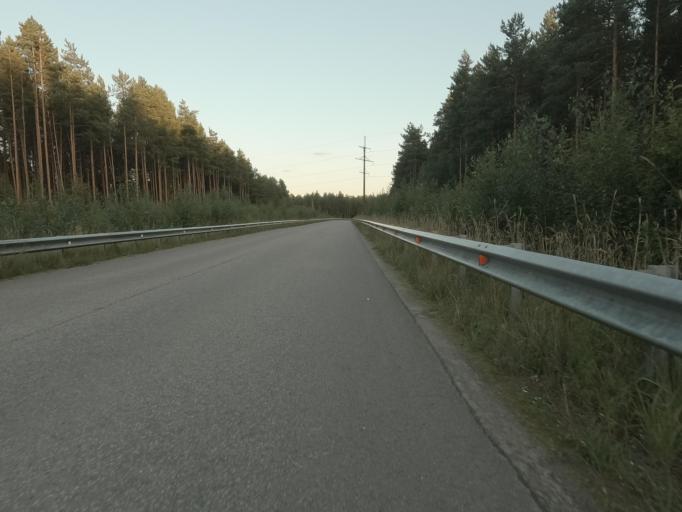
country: RU
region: Leningrad
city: Mga
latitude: 59.7633
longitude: 31.0382
